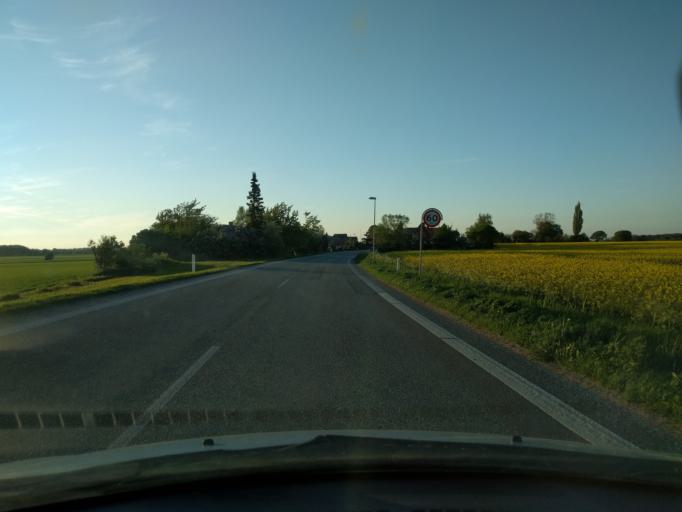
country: DK
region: Zealand
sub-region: Guldborgsund Kommune
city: Stubbekobing
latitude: 54.8093
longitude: 11.9928
